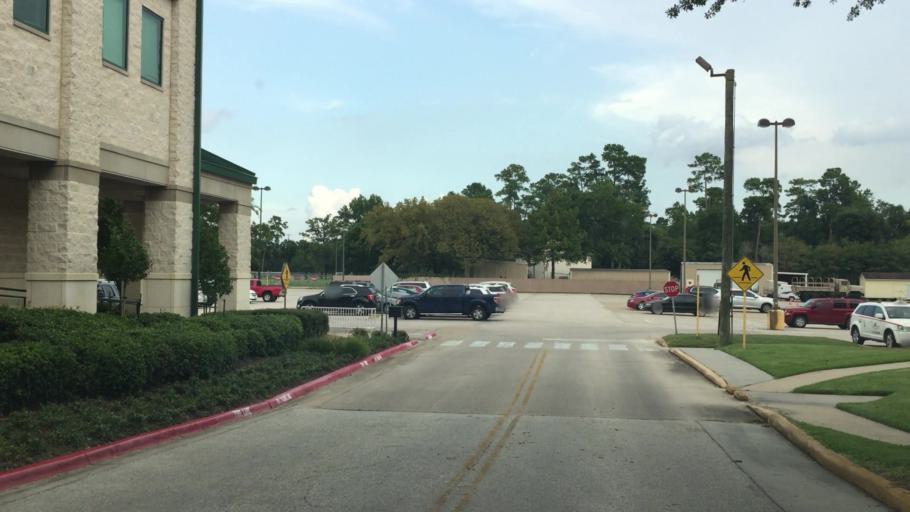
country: US
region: Texas
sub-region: Harris County
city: Hudson
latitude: 30.0122
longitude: -95.5098
